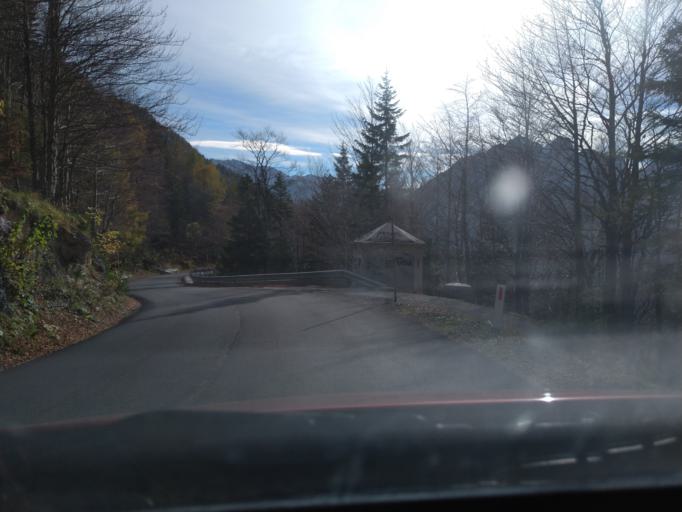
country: SI
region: Kranjska Gora
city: Kranjska Gora
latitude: 46.4256
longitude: 13.7436
